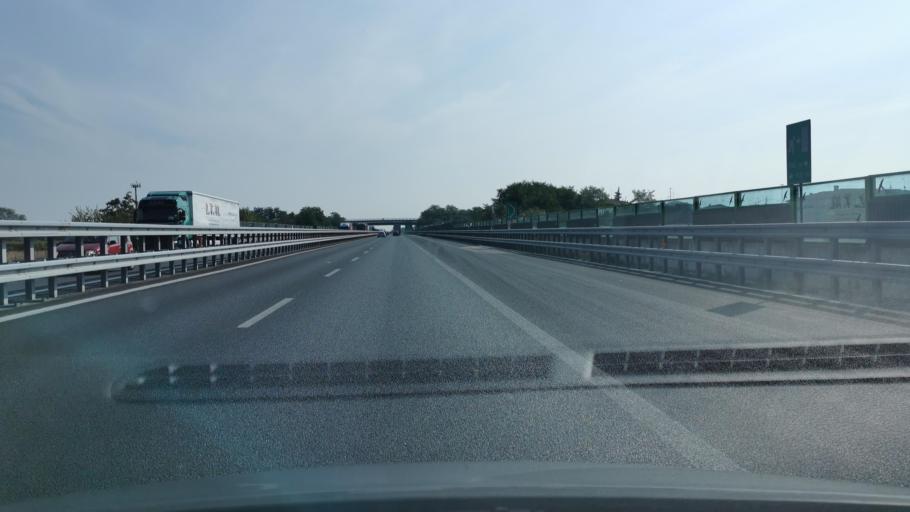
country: IT
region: Lombardy
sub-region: Provincia di Pavia
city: Stradella
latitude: 45.0828
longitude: 9.2988
